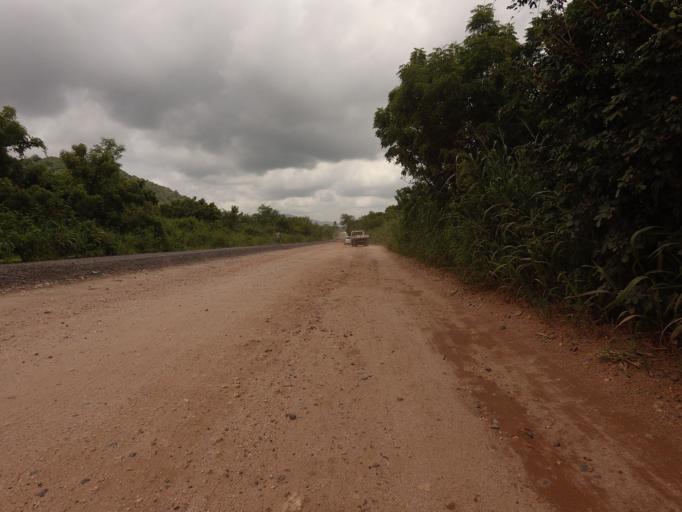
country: GH
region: Volta
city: Ho
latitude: 6.6541
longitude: 0.3021
